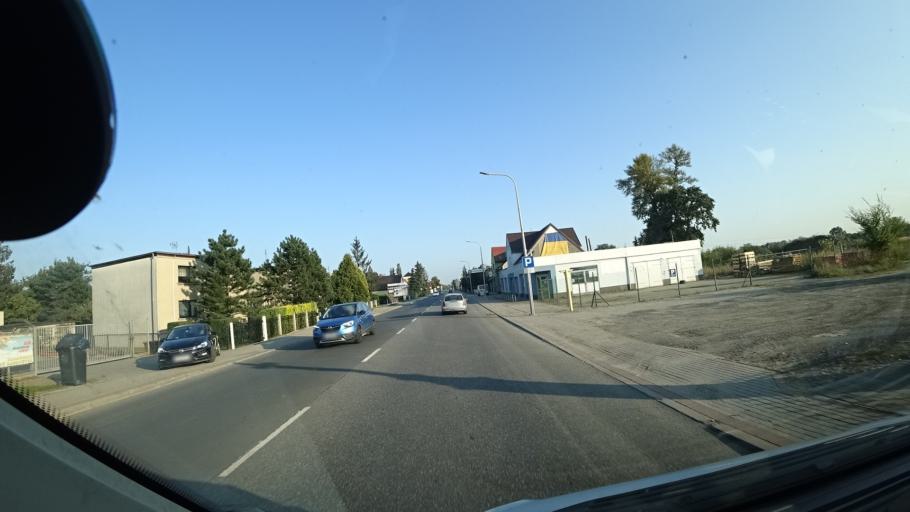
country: PL
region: Opole Voivodeship
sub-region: Powiat kedzierzynsko-kozielski
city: Kozle
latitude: 50.3432
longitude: 18.1715
